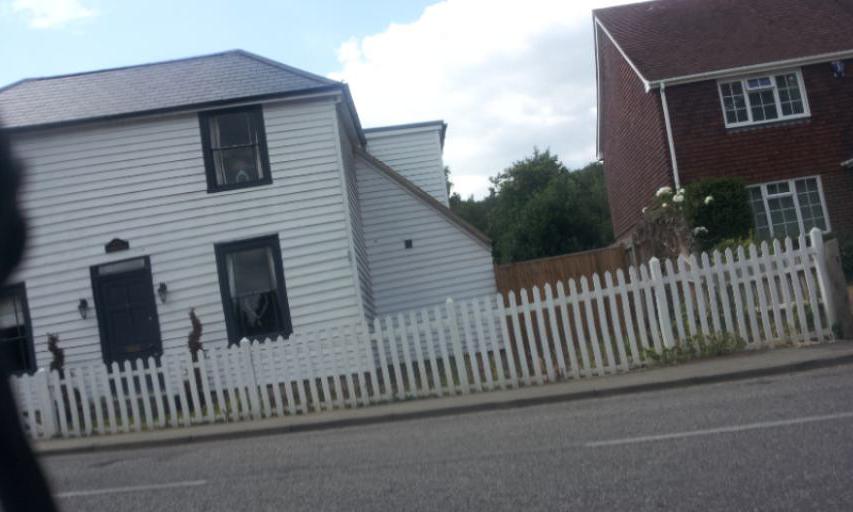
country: GB
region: England
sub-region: Kent
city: Harrietsham
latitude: 51.2086
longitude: 0.6796
